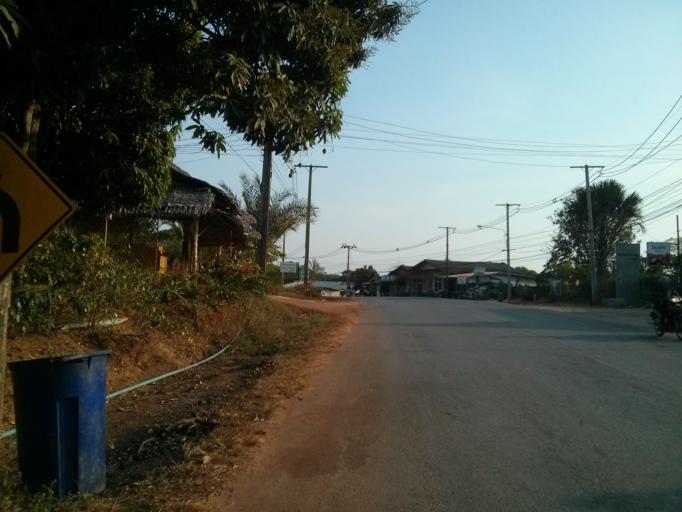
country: TH
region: Krabi
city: Saladan
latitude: 7.5951
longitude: 99.0352
